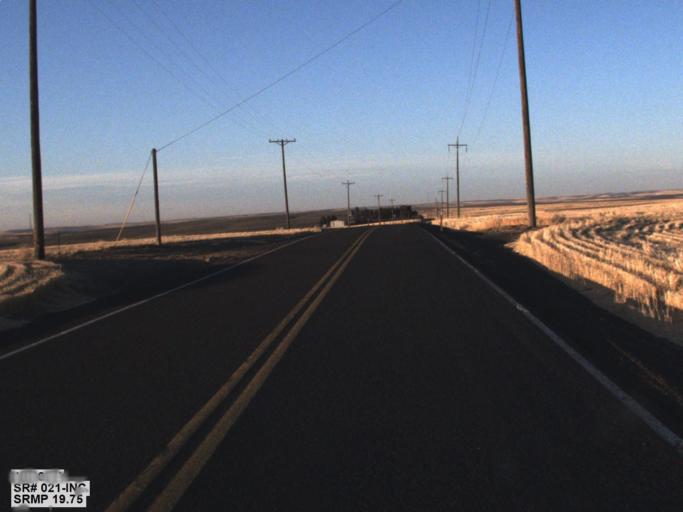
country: US
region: Washington
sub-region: Adams County
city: Ritzville
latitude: 46.9062
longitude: -118.5678
